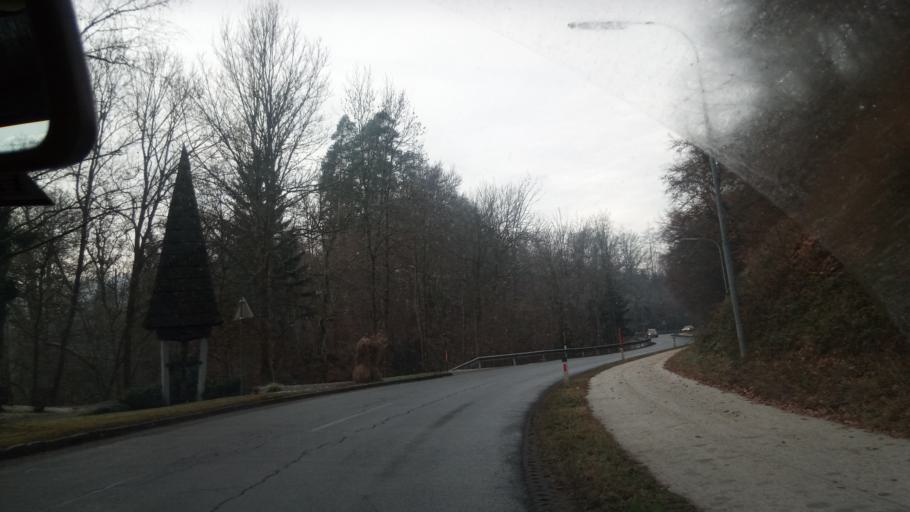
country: AT
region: Carinthia
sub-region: Politischer Bezirk Klagenfurt Land
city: Kottmannsdorf
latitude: 46.5912
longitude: 14.2671
